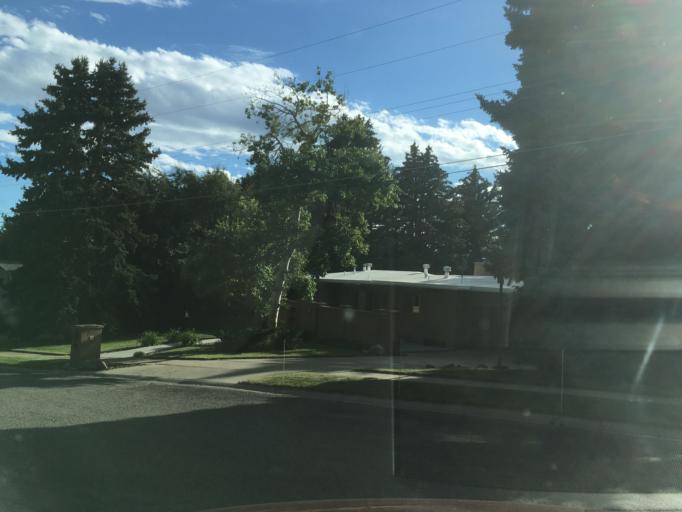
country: US
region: Montana
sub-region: Yellowstone County
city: Billings
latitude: 45.8005
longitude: -108.5794
